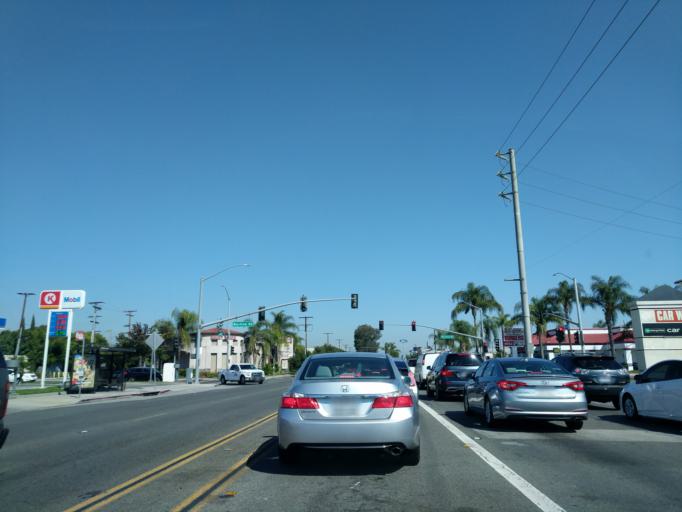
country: US
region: California
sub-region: Los Angeles County
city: Signal Hill
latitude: 33.8184
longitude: -118.1676
